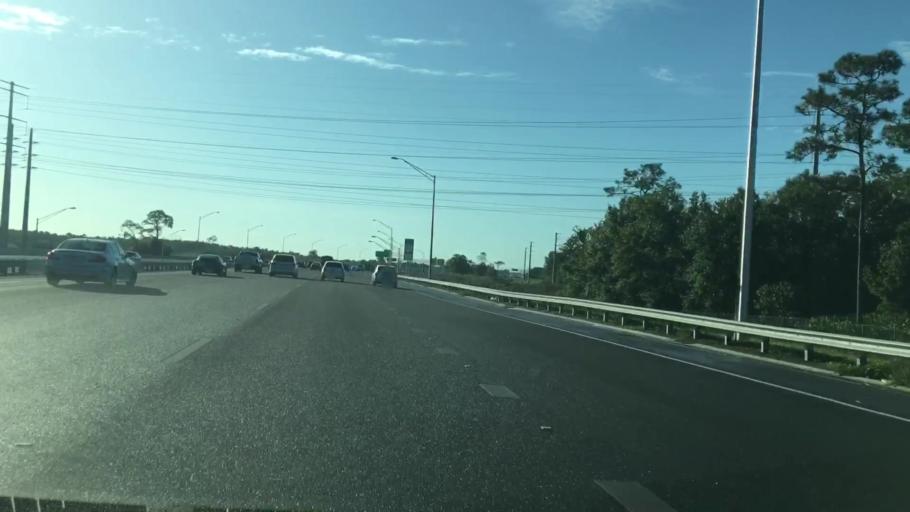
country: US
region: Florida
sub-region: Orange County
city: Azalea Park
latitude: 28.5038
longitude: -81.2452
